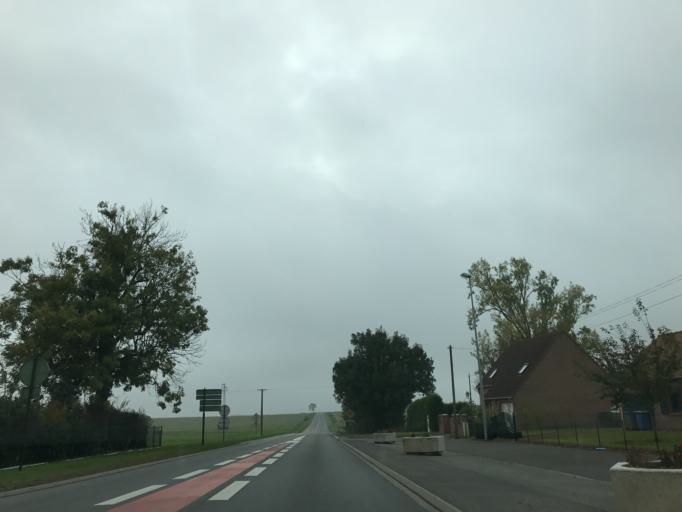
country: FR
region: Nord-Pas-de-Calais
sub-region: Departement du Pas-de-Calais
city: Beaurains
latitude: 50.2355
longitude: 2.8012
